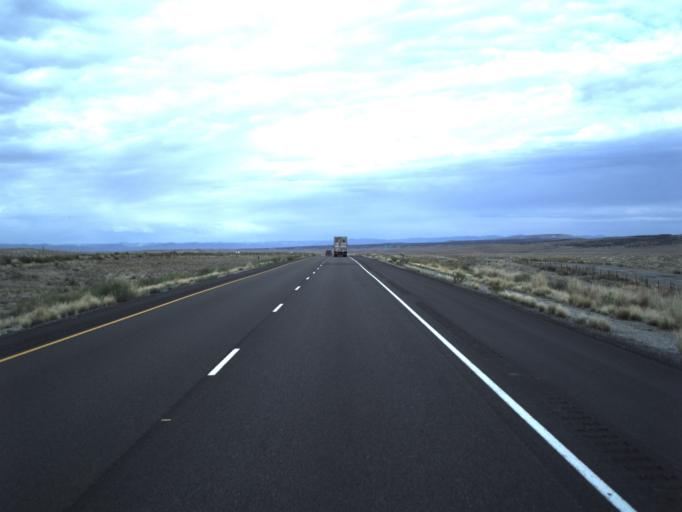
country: US
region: Colorado
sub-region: Mesa County
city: Loma
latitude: 39.0525
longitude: -109.2635
